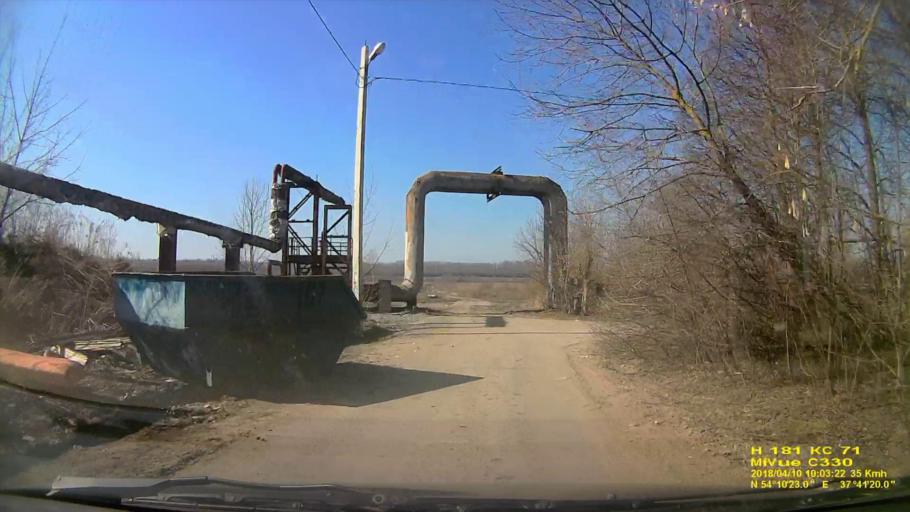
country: RU
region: Tula
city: Tula
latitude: 54.1729
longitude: 37.6890
